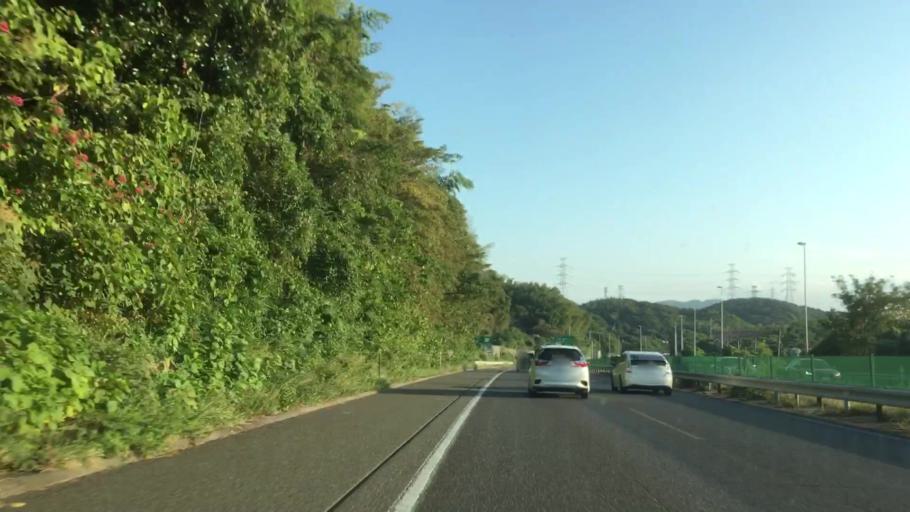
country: JP
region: Yamaguchi
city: Shimonoseki
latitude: 33.9831
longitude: 130.9521
